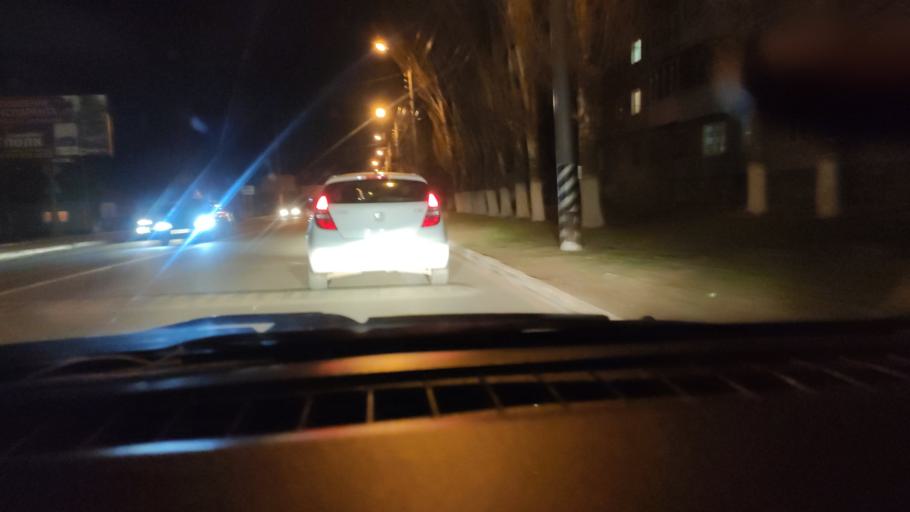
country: RU
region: Saratov
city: Privolzhskiy
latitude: 51.4085
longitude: 46.0406
